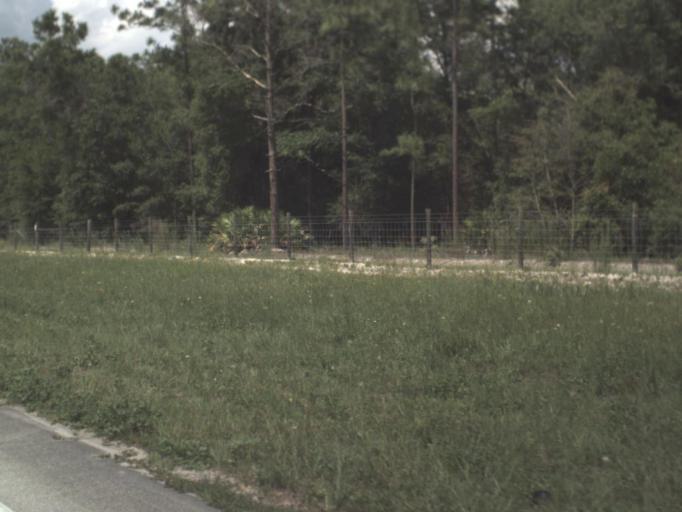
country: US
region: Florida
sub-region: Bradford County
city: Starke
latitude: 29.9514
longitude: -82.0163
